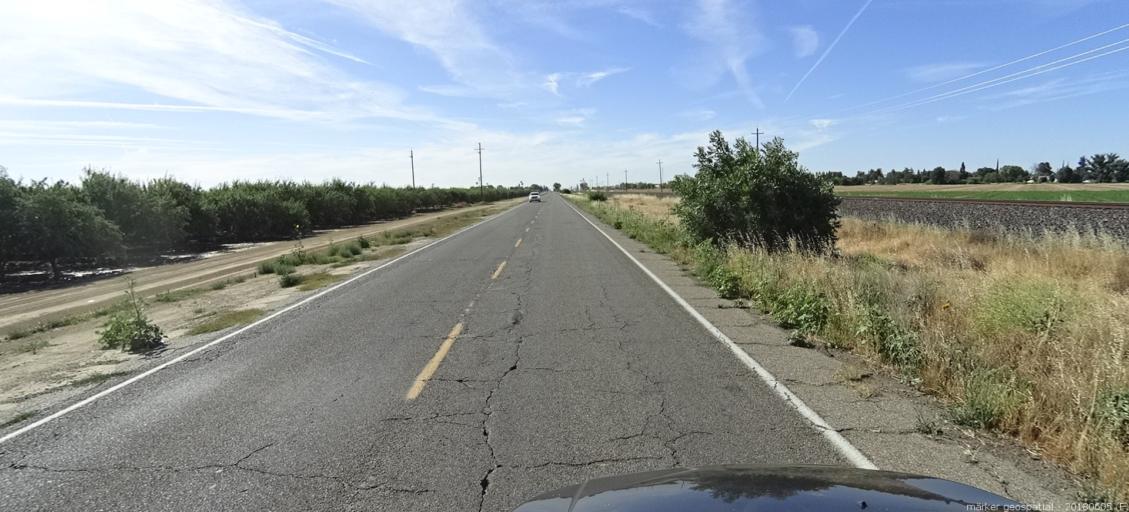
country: US
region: California
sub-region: Madera County
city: Chowchilla
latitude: 37.1326
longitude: -120.2664
